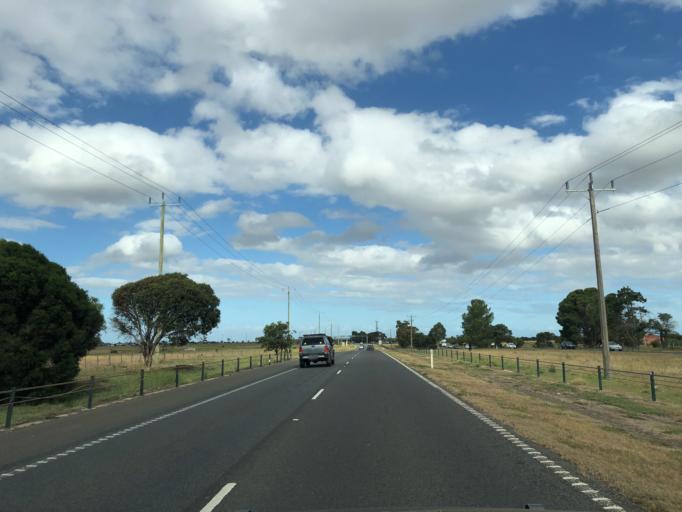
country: AU
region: Victoria
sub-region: Melton
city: Rockbank
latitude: -37.7173
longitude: 144.6422
